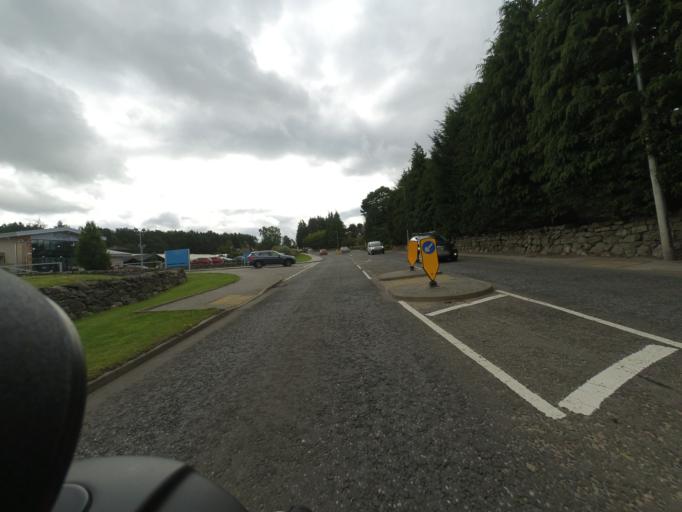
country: GB
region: Scotland
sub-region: Aberdeenshire
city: Banchory
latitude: 57.0619
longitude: -2.4958
